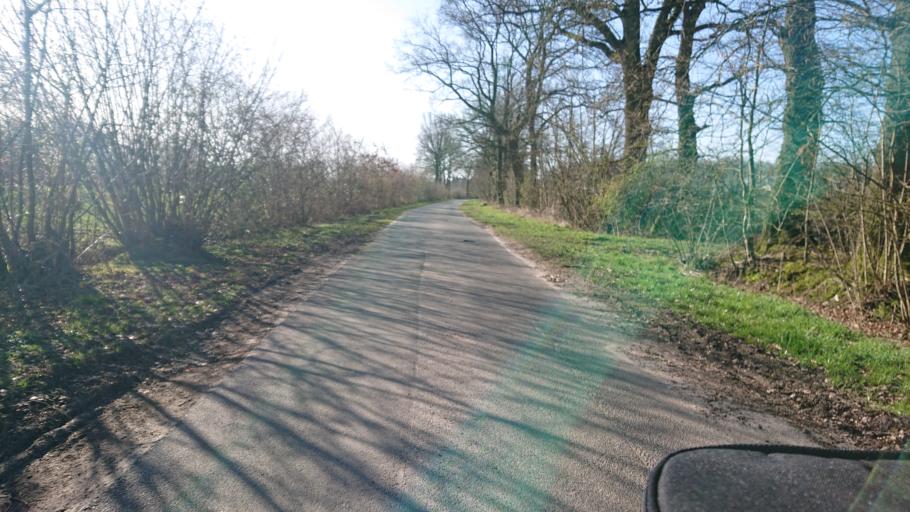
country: DE
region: Schleswig-Holstein
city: Hasloh
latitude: 53.6894
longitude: 9.9025
